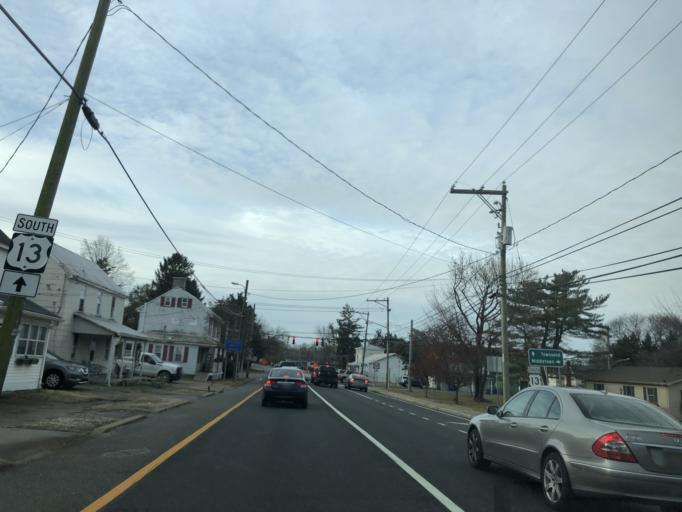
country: US
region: Delaware
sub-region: New Castle County
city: Middletown
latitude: 39.4579
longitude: -75.6613
